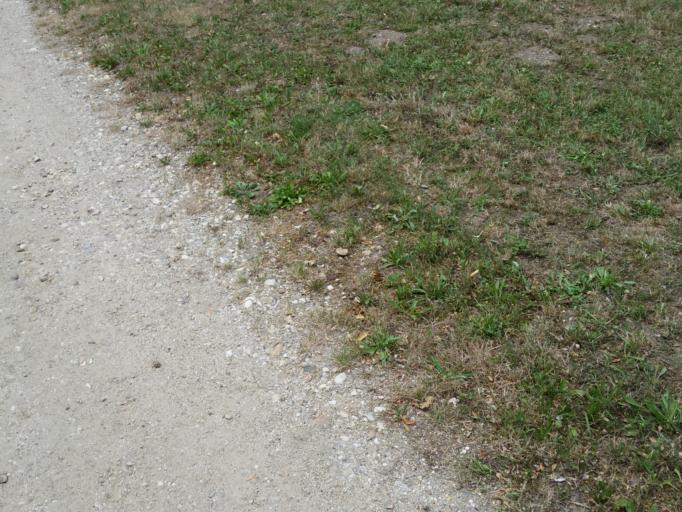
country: HU
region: Vas
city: Repcelak
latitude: 47.4540
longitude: 17.0365
